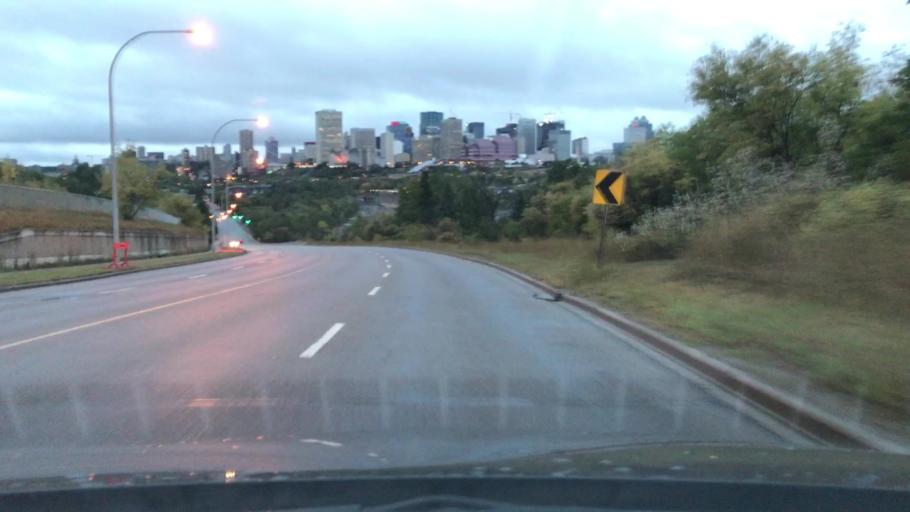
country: CA
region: Alberta
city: Edmonton
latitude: 53.5383
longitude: -113.4605
